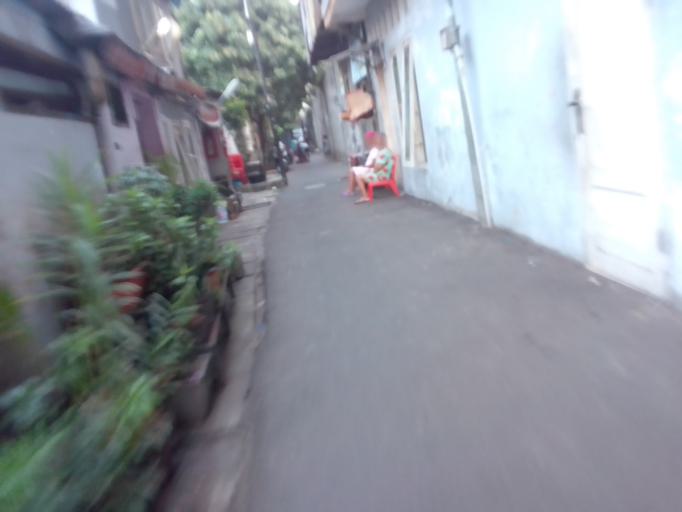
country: ID
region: Jakarta Raya
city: Jakarta
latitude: -6.2007
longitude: 106.8089
